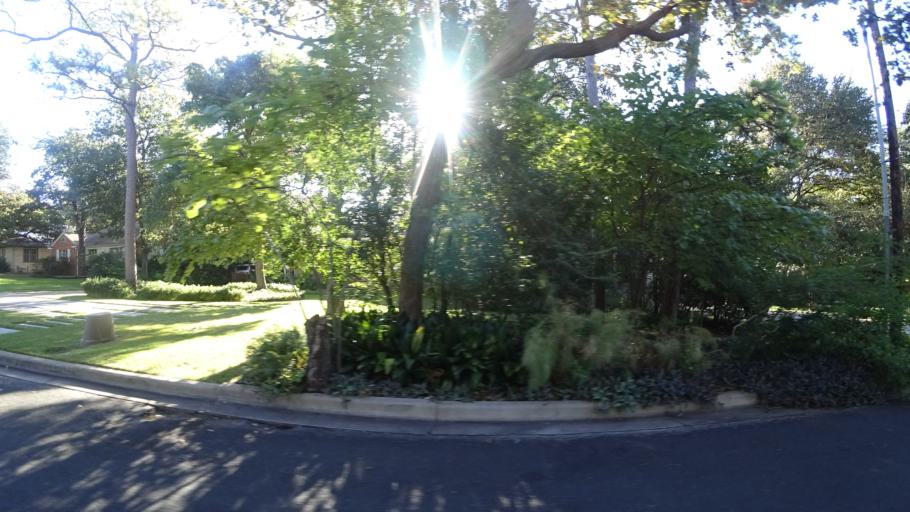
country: US
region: Texas
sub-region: Travis County
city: Rollingwood
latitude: 30.2873
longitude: -97.7694
